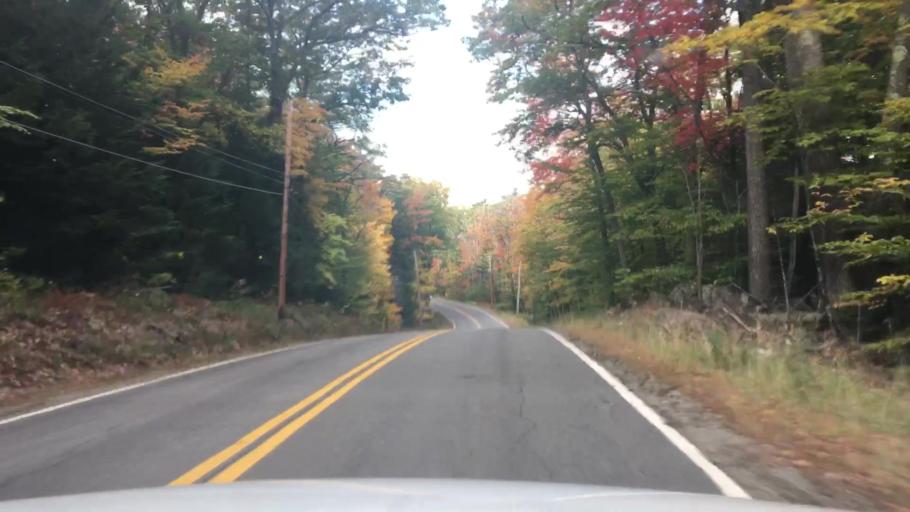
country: US
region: Maine
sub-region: Knox County
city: Hope
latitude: 44.2410
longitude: -69.1137
